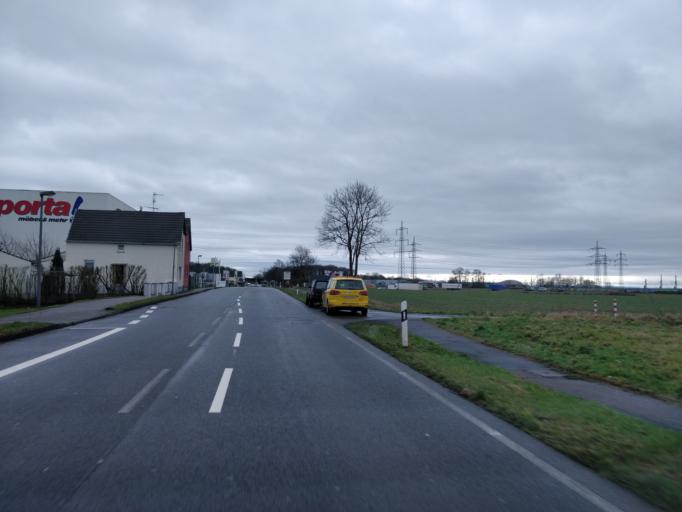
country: DE
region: North Rhine-Westphalia
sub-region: Regierungsbezirk Koln
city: Wahn-Heide
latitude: 50.8500
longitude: 7.0919
